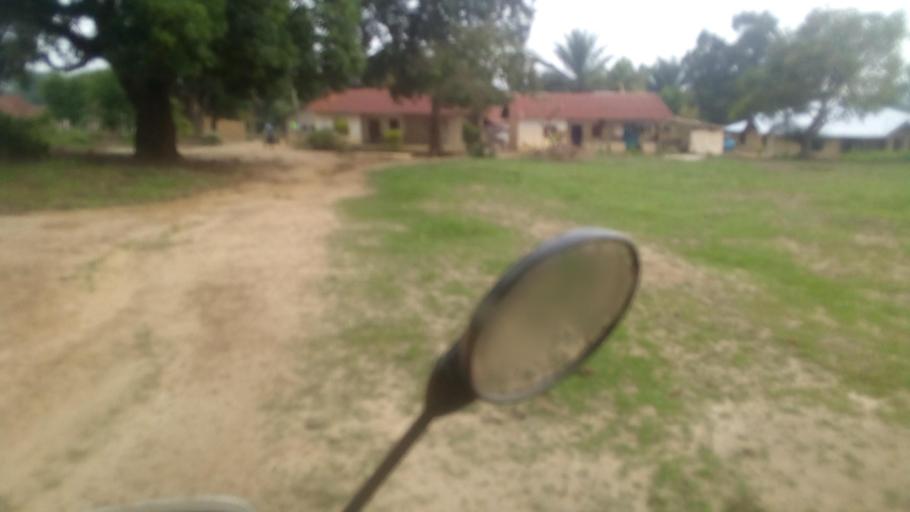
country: SL
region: Eastern Province
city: Pendembu
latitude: 8.0953
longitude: -10.6973
